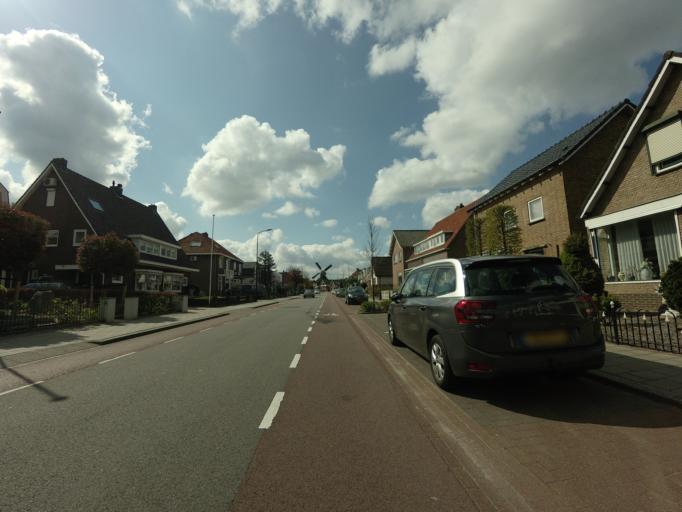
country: NL
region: Utrecht
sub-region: Gemeente Veenendaal
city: Veenendaal
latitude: 52.0366
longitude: 5.5533
